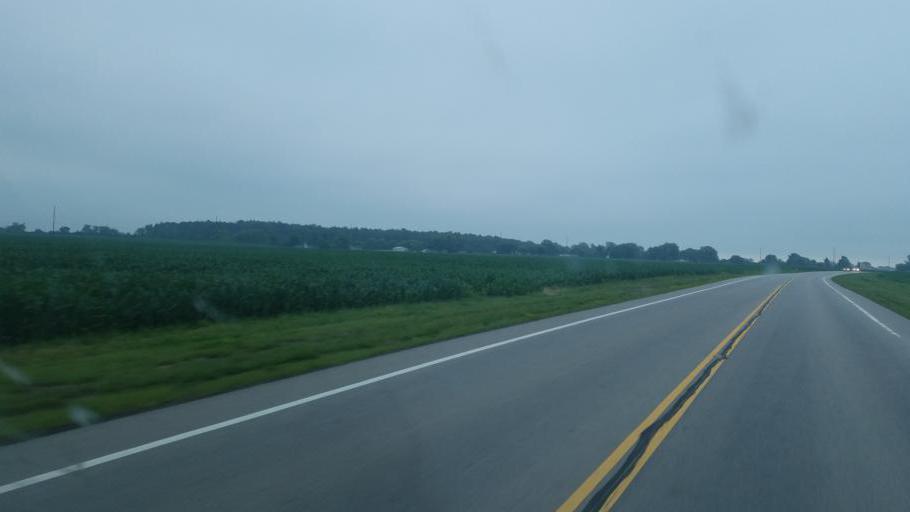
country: US
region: Ohio
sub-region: Fayette County
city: Washington Court House
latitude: 39.5588
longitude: -83.4023
